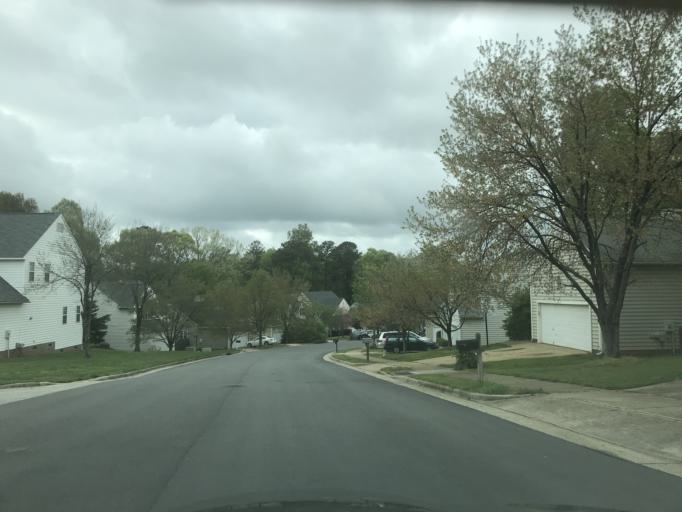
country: US
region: North Carolina
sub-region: Wake County
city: West Raleigh
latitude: 35.7474
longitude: -78.6851
